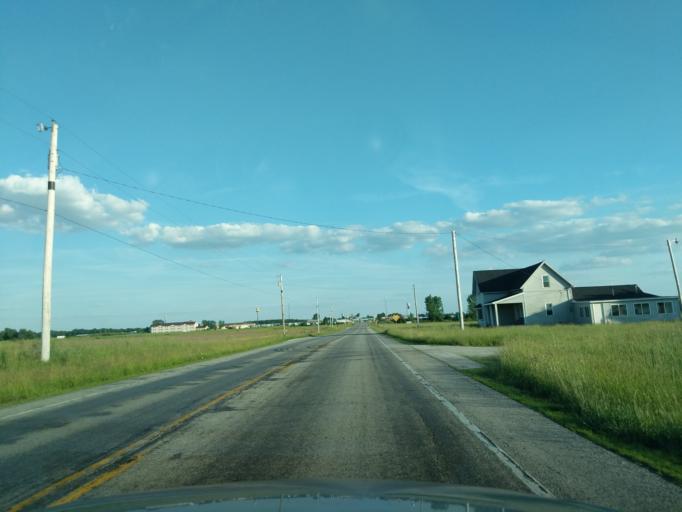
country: US
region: Indiana
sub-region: Huntington County
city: Warren
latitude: 40.7285
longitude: -85.4393
